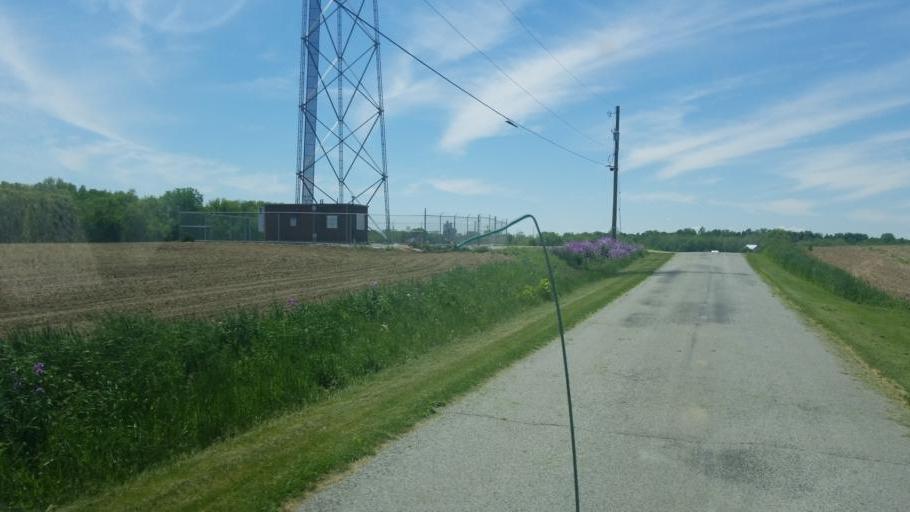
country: US
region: Ohio
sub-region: Huron County
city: Norwalk
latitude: 41.1195
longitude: -82.6137
